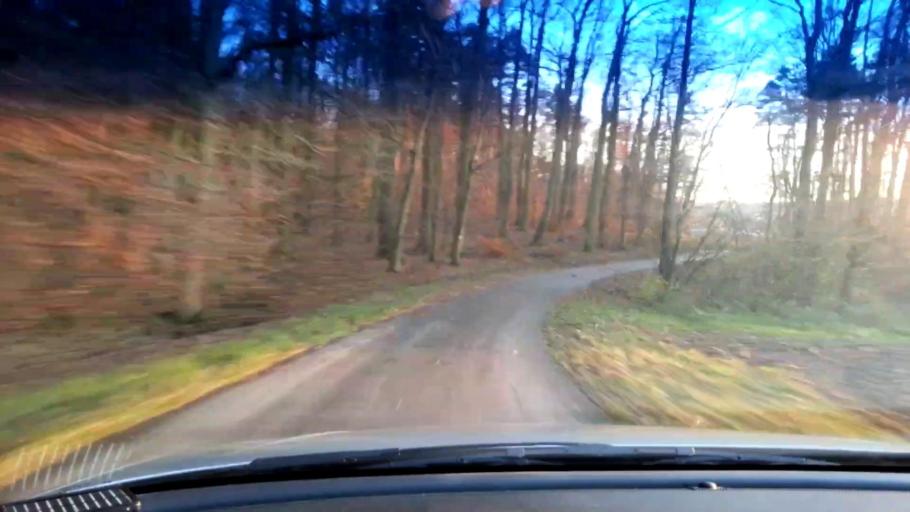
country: DE
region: Bavaria
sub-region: Upper Franconia
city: Zapfendorf
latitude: 50.0285
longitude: 10.9441
